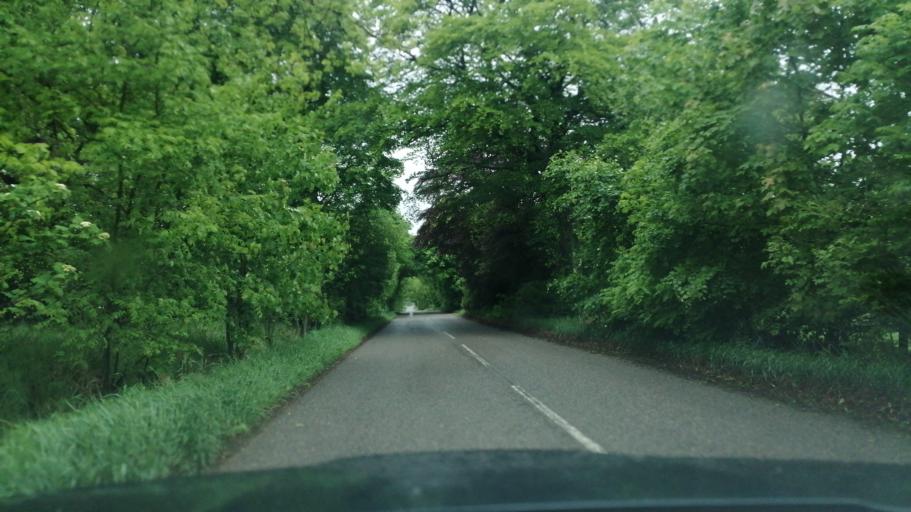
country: GB
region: Scotland
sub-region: Aberdeenshire
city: Huntly
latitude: 57.5424
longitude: -2.7952
